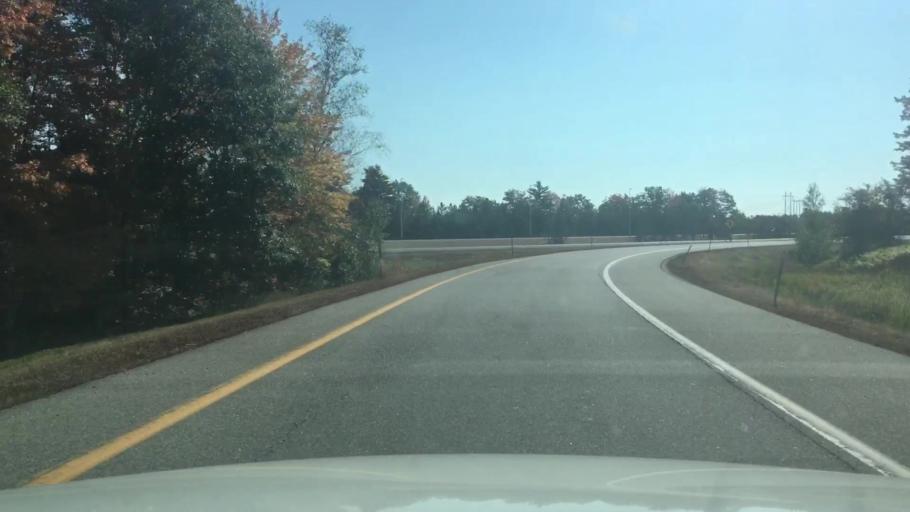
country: US
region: Maine
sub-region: Sagadahoc County
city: Topsham
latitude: 43.9401
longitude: -69.9825
